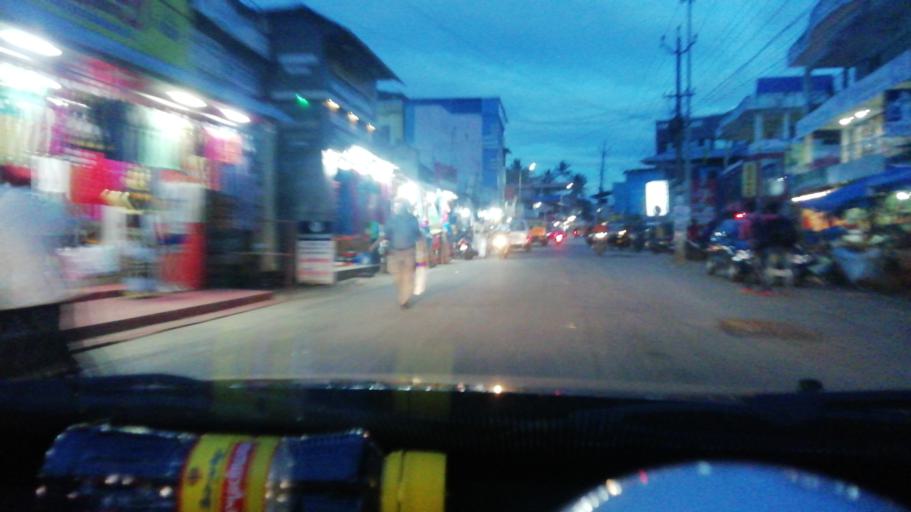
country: IN
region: Kerala
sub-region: Thiruvananthapuram
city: Paravur
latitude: 8.8106
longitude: 76.6708
